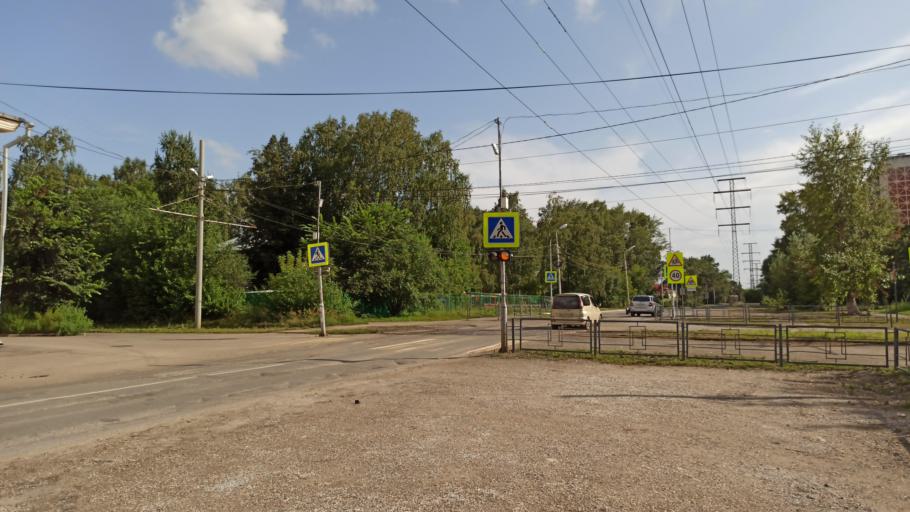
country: RU
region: Tomsk
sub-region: Tomskiy Rayon
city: Tomsk
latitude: 56.4791
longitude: 84.9996
